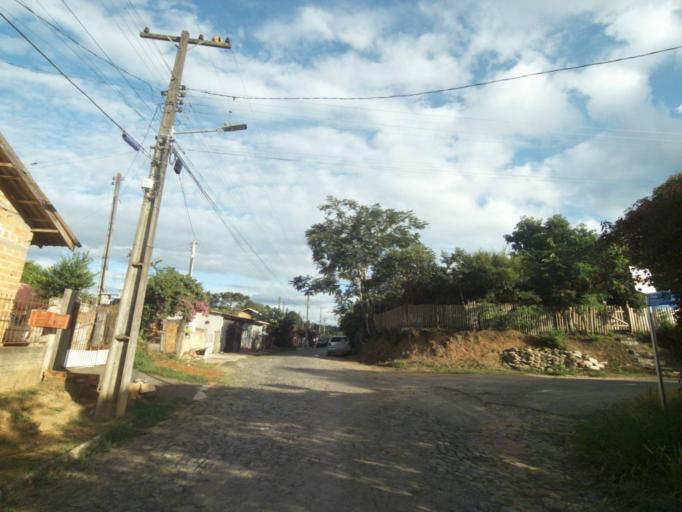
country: BR
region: Parana
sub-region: Telemaco Borba
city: Telemaco Borba
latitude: -24.3233
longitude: -50.6097
